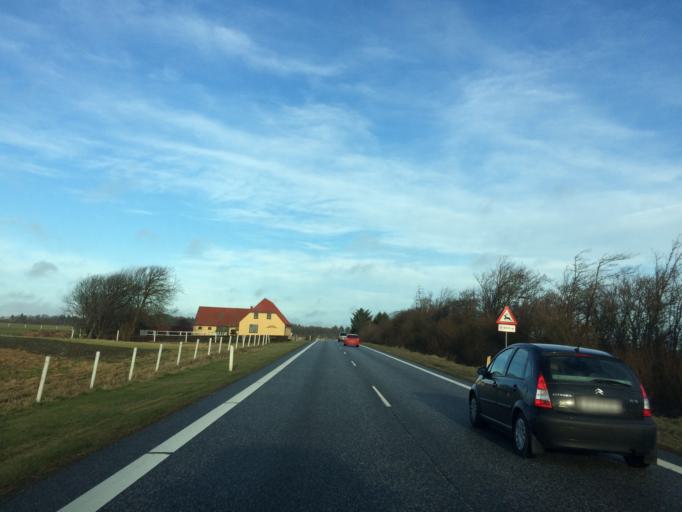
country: DK
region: North Denmark
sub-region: Thisted Kommune
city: Hurup
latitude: 56.8294
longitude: 8.5039
